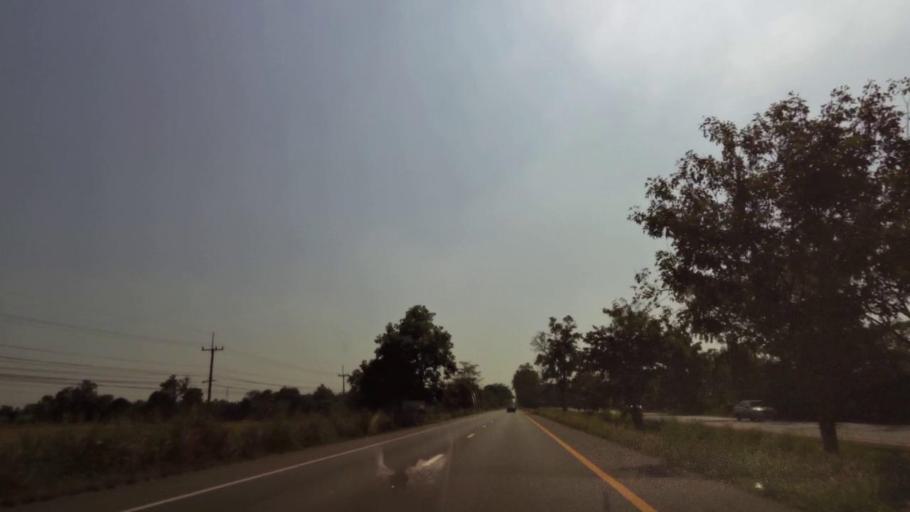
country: TH
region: Nakhon Sawan
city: Banphot Phisai
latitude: 16.0046
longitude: 100.1158
